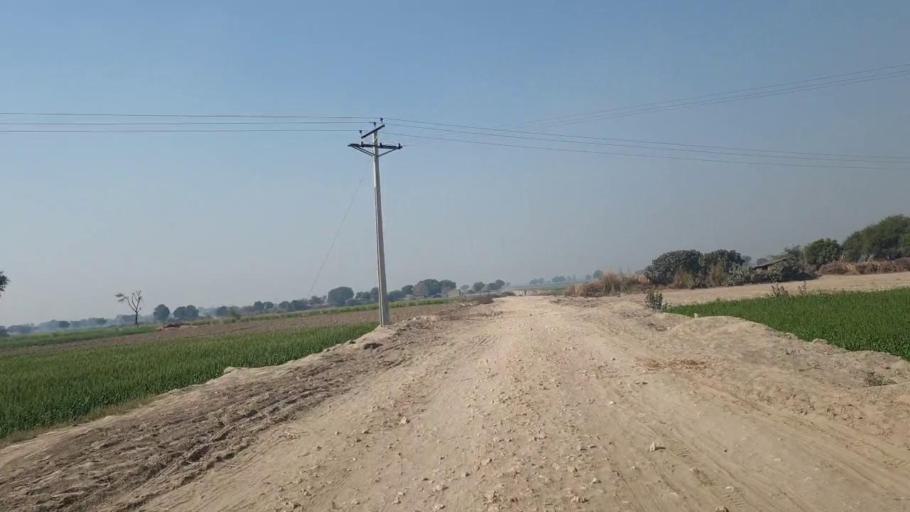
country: PK
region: Sindh
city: Shahpur Chakar
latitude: 26.1095
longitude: 68.6021
